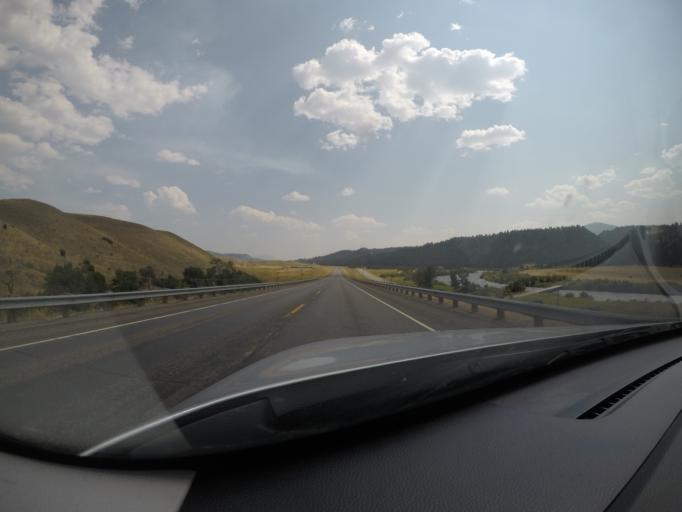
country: US
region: Montana
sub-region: Gallatin County
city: Big Sky
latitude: 44.9770
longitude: -111.6457
